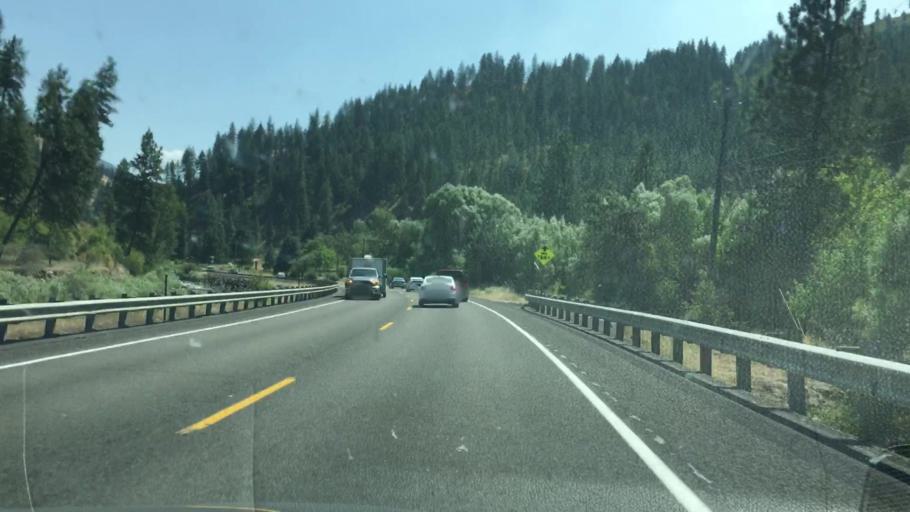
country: US
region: Idaho
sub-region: Valley County
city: McCall
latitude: 45.2406
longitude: -116.3317
